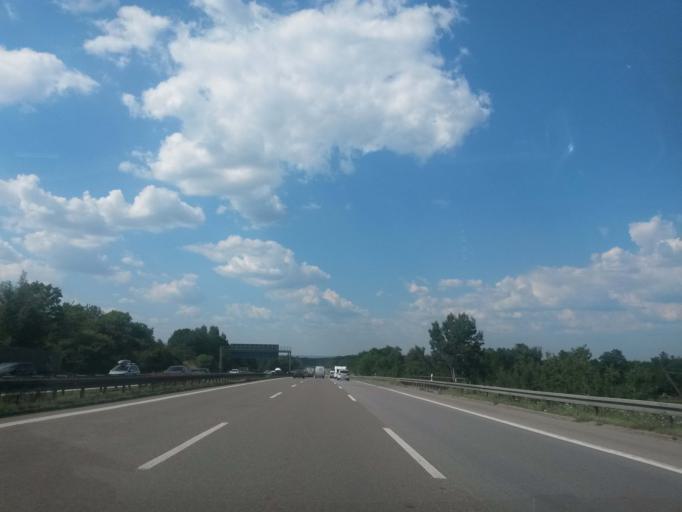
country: DE
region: Bavaria
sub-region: Upper Bavaria
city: Reichertshofen
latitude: 48.6522
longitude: 11.5139
